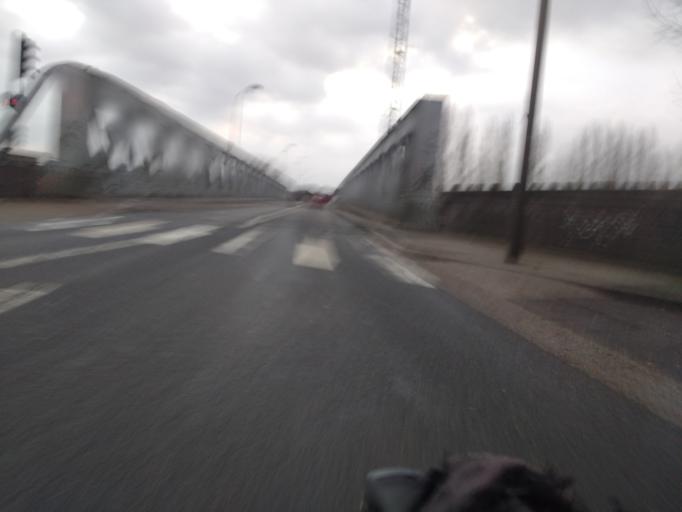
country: FR
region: Picardie
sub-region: Departement de la Somme
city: Longueau
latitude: 49.8750
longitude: 2.3485
